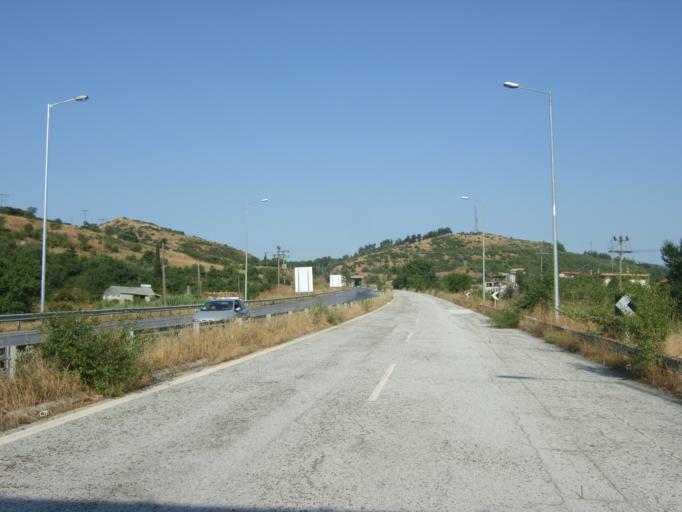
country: GR
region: Central Macedonia
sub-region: Nomos Thessalonikis
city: Lagyna
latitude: 40.7293
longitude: 22.9968
